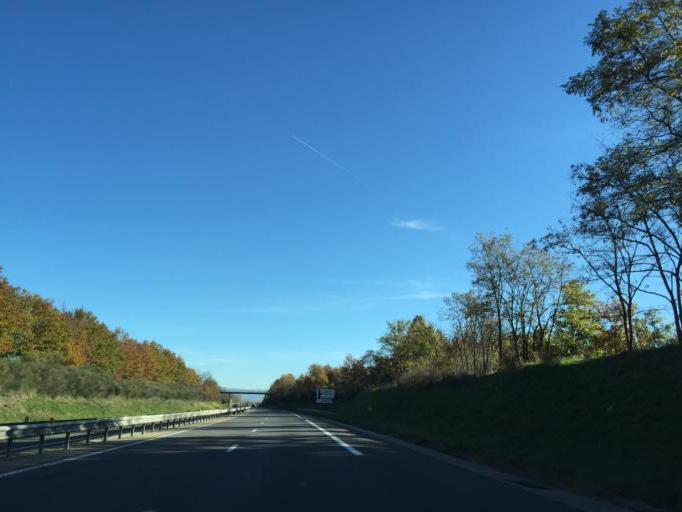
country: FR
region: Rhone-Alpes
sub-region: Departement de la Loire
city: Montrond-les-Bains
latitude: 45.6561
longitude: 4.1690
